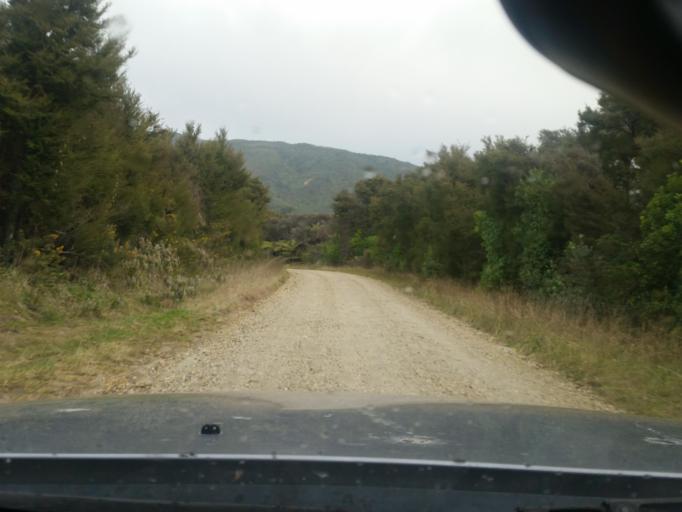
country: NZ
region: Tasman
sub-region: Tasman District
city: Takaka
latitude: -40.7322
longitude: 172.6880
